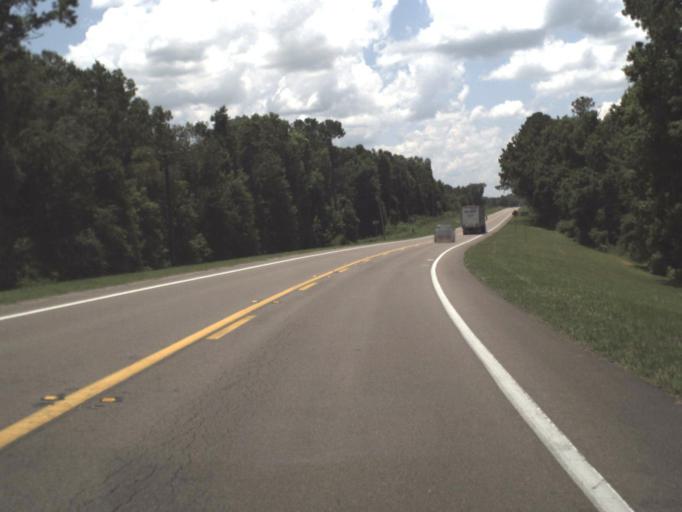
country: US
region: Florida
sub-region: Alachua County
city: Alachua
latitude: 29.8733
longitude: -82.4117
